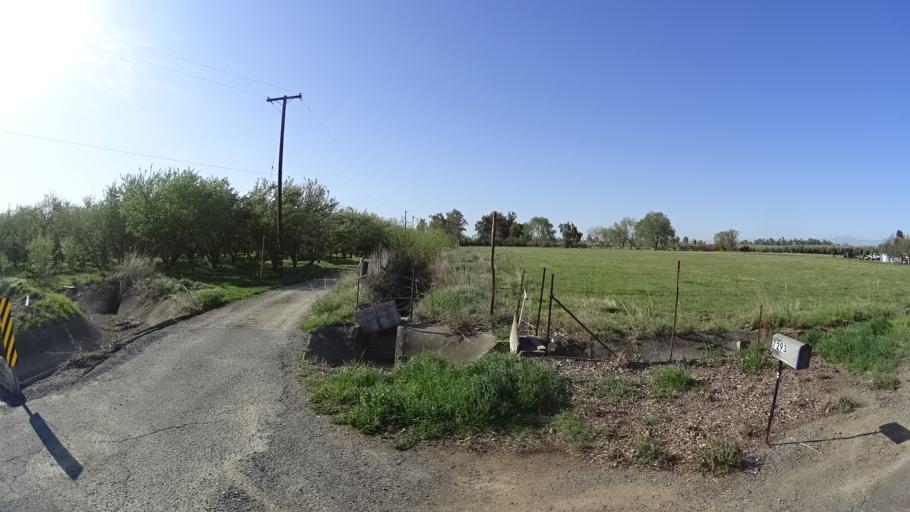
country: US
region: California
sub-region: Glenn County
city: Orland
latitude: 39.7573
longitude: -122.1087
